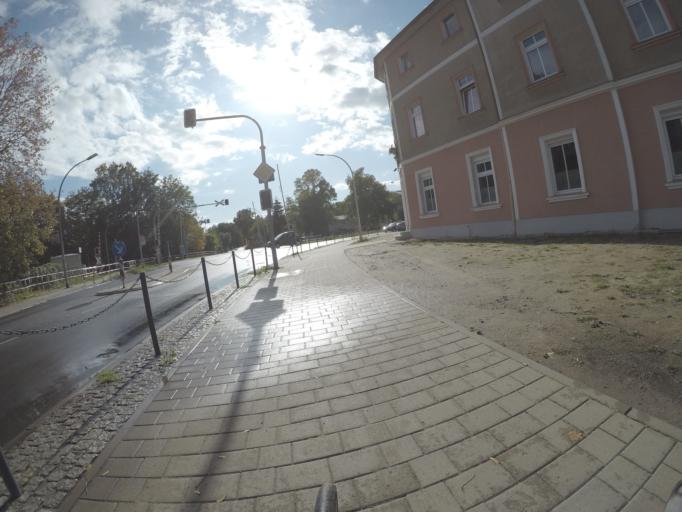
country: DE
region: Brandenburg
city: Petershagen
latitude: 52.5320
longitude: 13.8441
